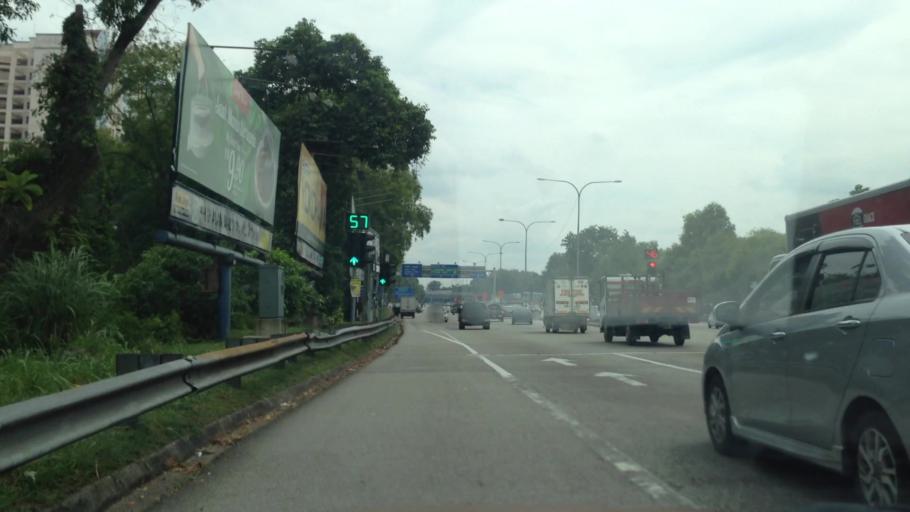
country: MY
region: Selangor
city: Shah Alam
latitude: 3.0780
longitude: 101.5551
